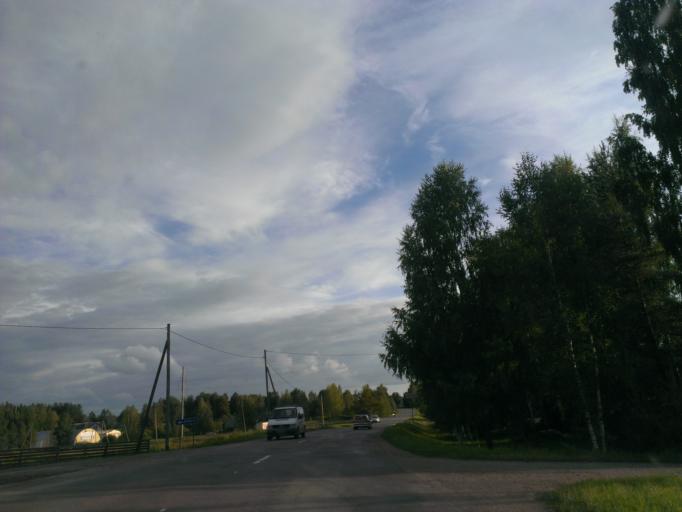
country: LV
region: Ikskile
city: Ikskile
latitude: 56.8474
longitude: 24.5040
